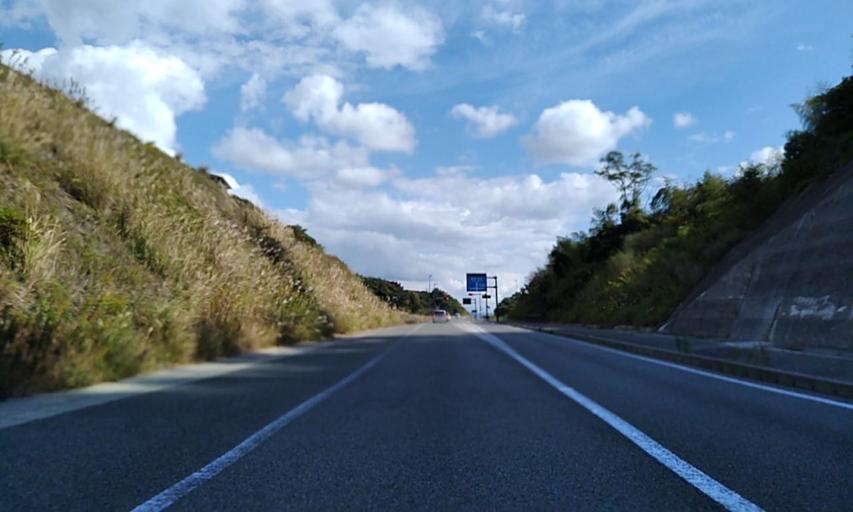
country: JP
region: Wakayama
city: Tanabe
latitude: 33.7498
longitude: 135.3592
